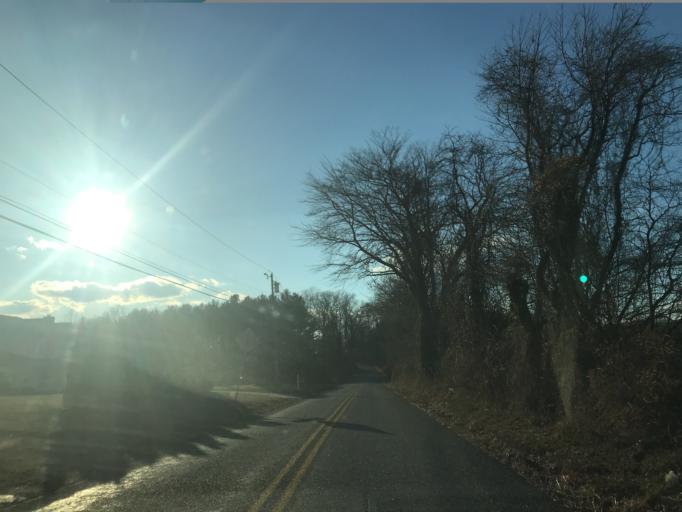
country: US
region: Pennsylvania
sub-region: York County
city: Susquehanna Trails
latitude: 39.6798
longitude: -76.2311
